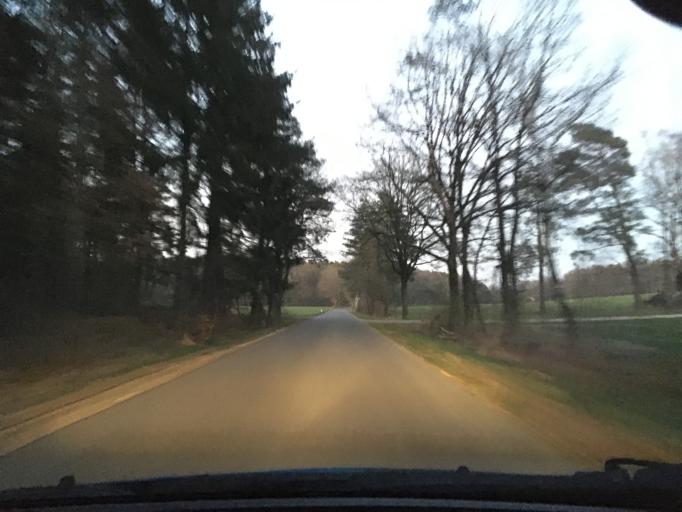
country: DE
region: Lower Saxony
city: Wriedel
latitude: 53.0737
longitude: 10.2709
